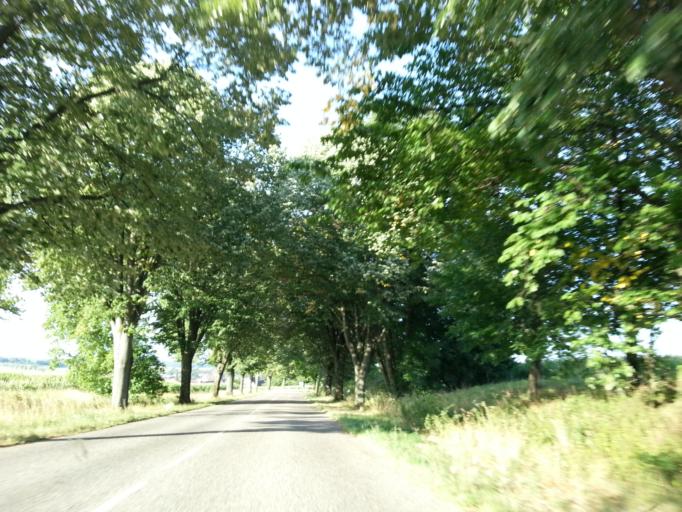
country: FR
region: Alsace
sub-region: Departement du Bas-Rhin
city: Soultz-sous-Forets
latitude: 48.9297
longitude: 7.8734
